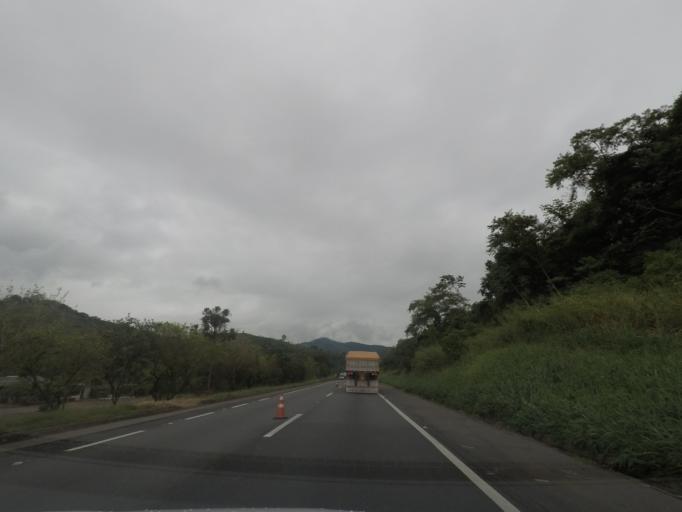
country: BR
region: Sao Paulo
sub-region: Cajati
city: Cajati
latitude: -24.8111
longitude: -48.2109
